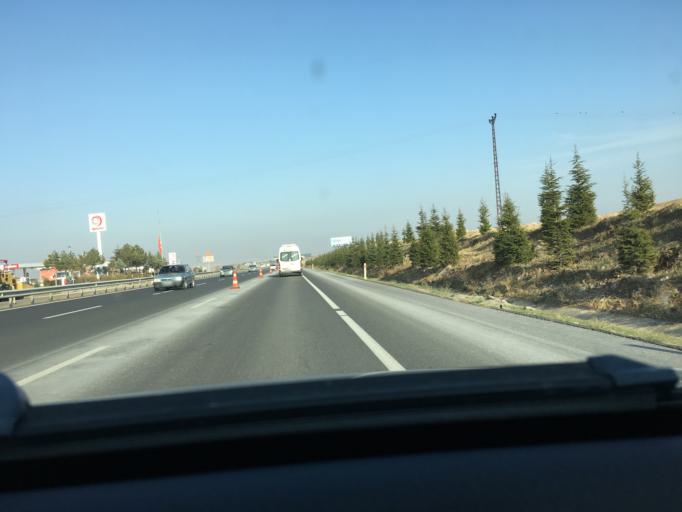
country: TR
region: Ankara
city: Temelli
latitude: 39.7056
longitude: 32.2790
